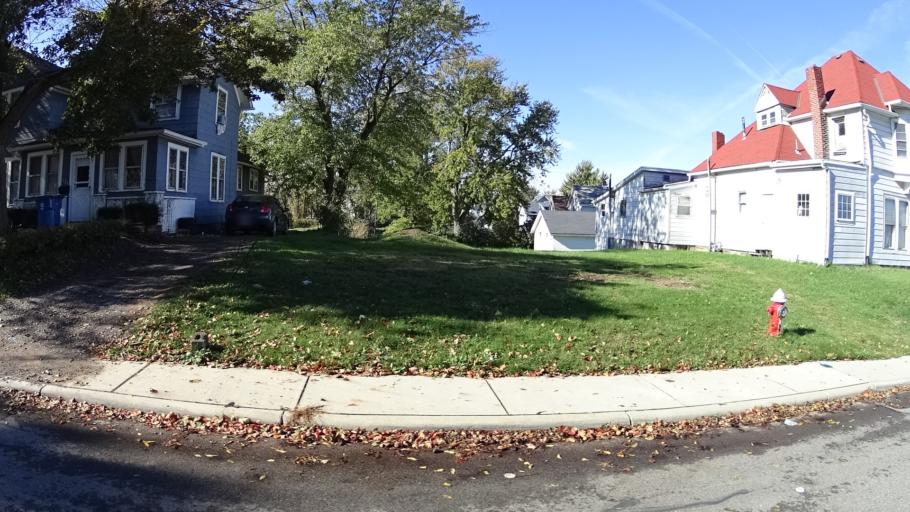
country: US
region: Ohio
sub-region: Lorain County
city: Lorain
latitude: 41.4695
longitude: -82.1817
